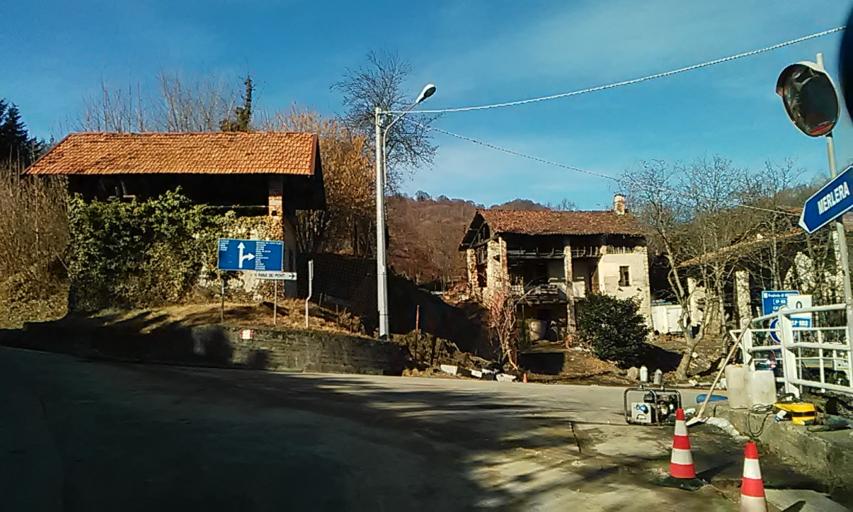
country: IT
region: Piedmont
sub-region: Provincia di Vercelli
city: Cellio
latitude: 45.7573
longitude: 8.3114
